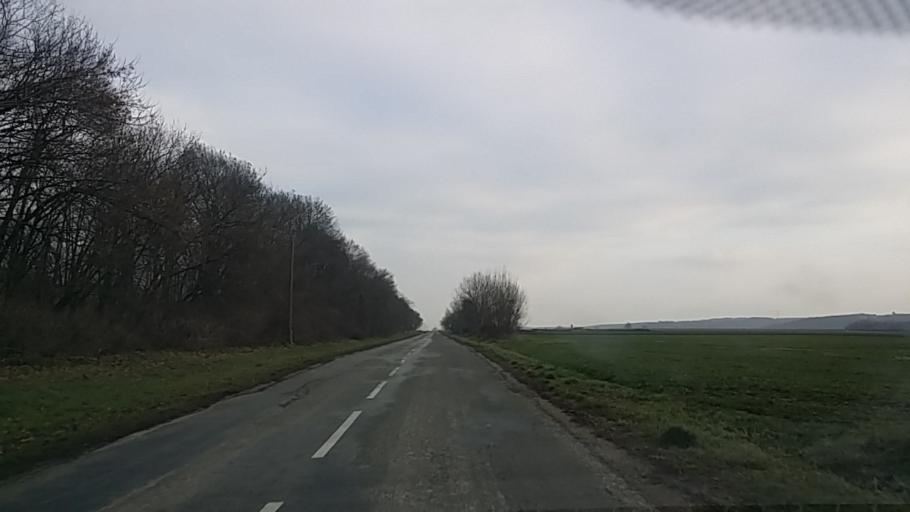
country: HU
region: Baranya
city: Lanycsok
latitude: 46.0956
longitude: 18.5553
